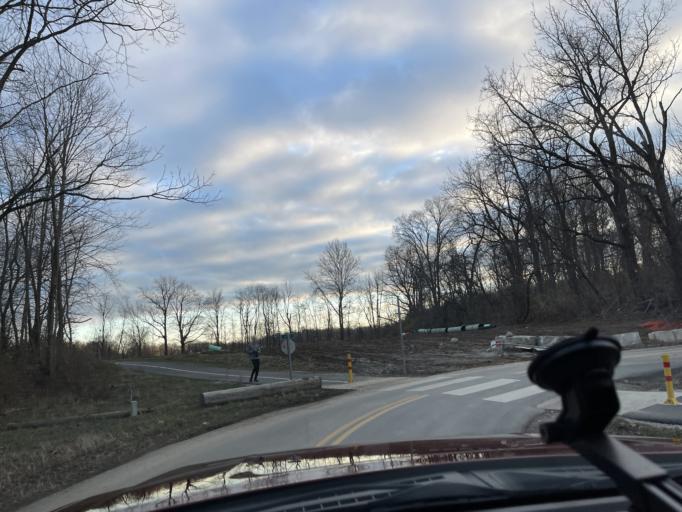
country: US
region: Indiana
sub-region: Hendricks County
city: Avon
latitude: 39.7737
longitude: -86.4206
